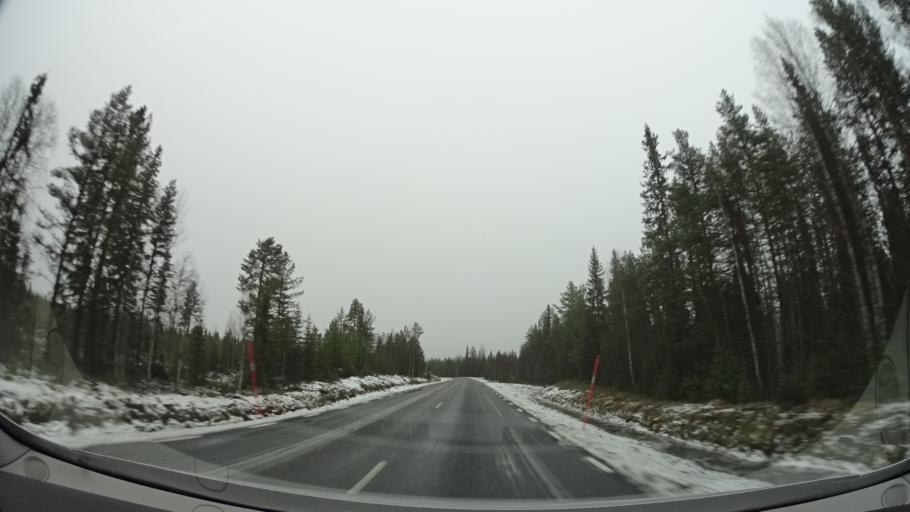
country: SE
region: Vaesterbotten
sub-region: Asele Kommun
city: Insjon
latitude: 64.2514
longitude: 17.5502
